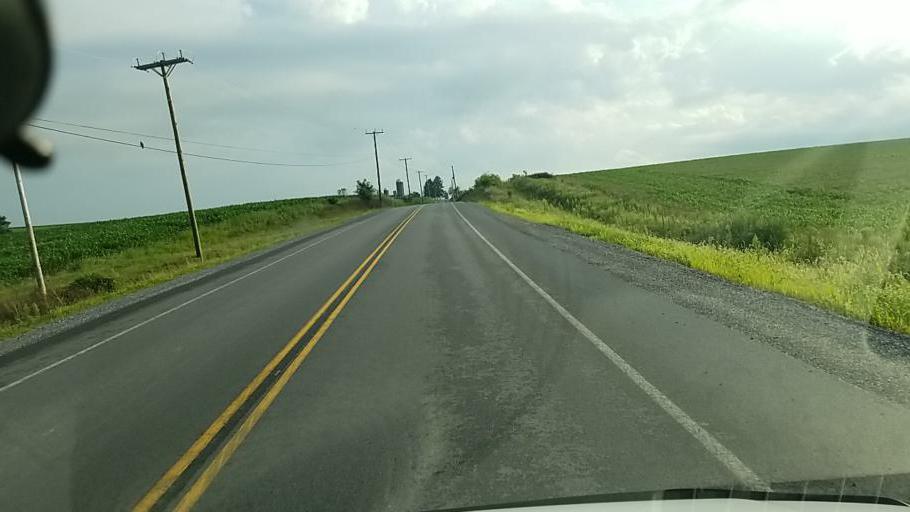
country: US
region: Pennsylvania
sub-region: Cumberland County
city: Shippensburg
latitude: 40.1730
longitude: -77.5447
